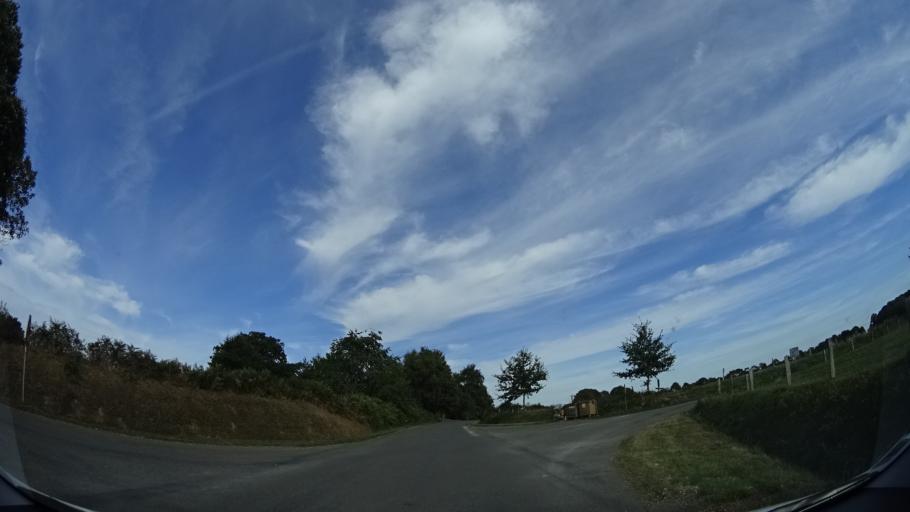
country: FR
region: Brittany
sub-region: Departement d'Ille-et-Vilaine
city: Romagne
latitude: 48.3341
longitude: -1.2487
